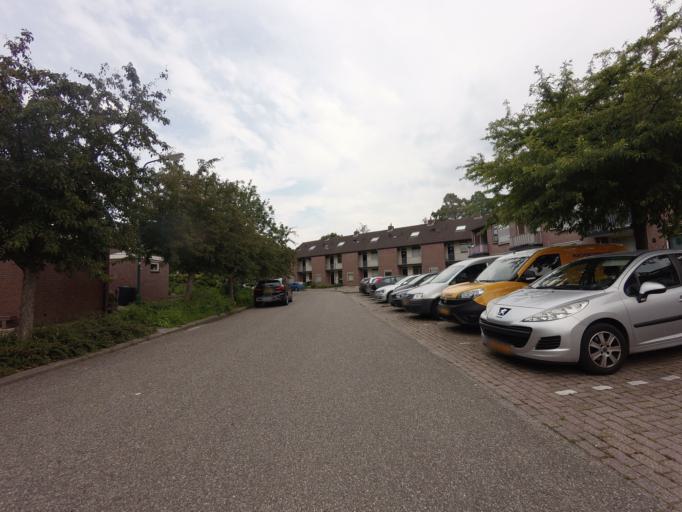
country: NL
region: Utrecht
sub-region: Stichtse Vecht
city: Breukelen
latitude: 52.1524
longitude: 4.9500
